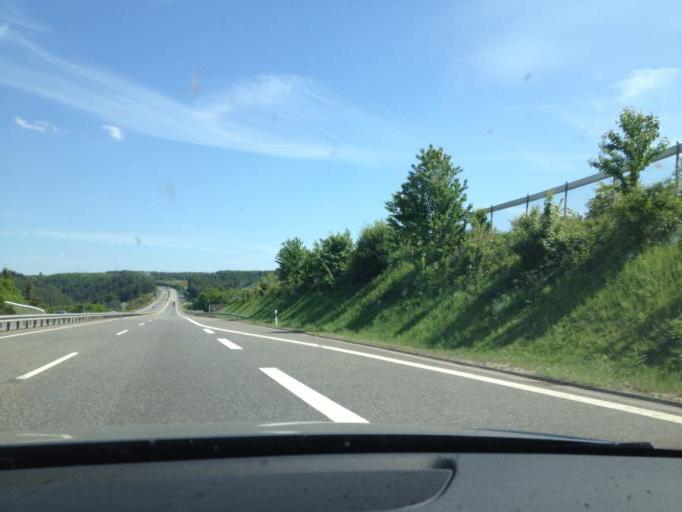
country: DE
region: Rheinland-Pfalz
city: Landscheid
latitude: 49.9895
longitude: 6.7840
